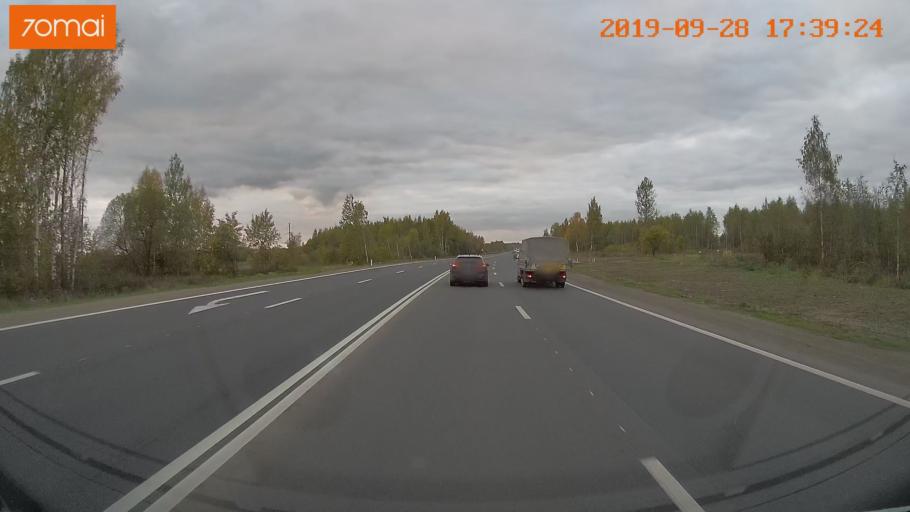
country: RU
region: Jaroslavl
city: Yaroslavl
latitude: 57.5444
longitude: 39.9212
